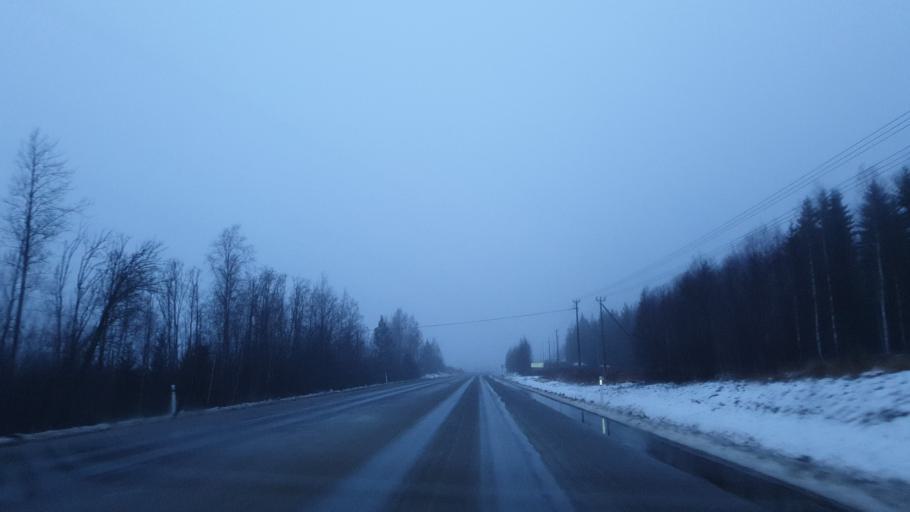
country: SE
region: Vaesterbotten
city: Obbola
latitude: 63.7751
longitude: 20.3296
